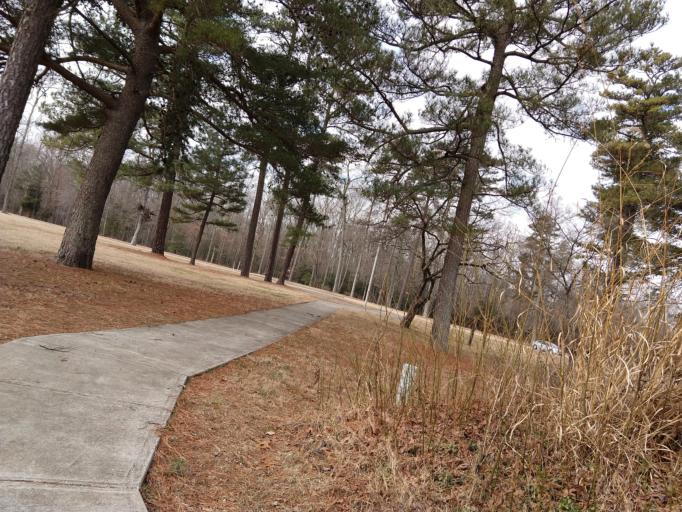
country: US
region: Virginia
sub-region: Chesterfield County
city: Bellwood
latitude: 37.4279
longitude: -77.3726
